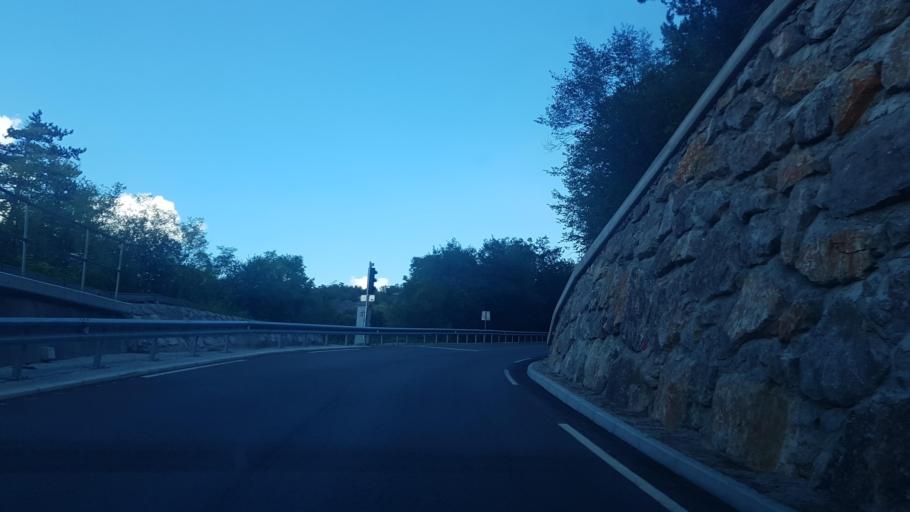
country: SI
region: Ajdovscina
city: Lokavec
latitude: 45.8377
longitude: 13.8286
